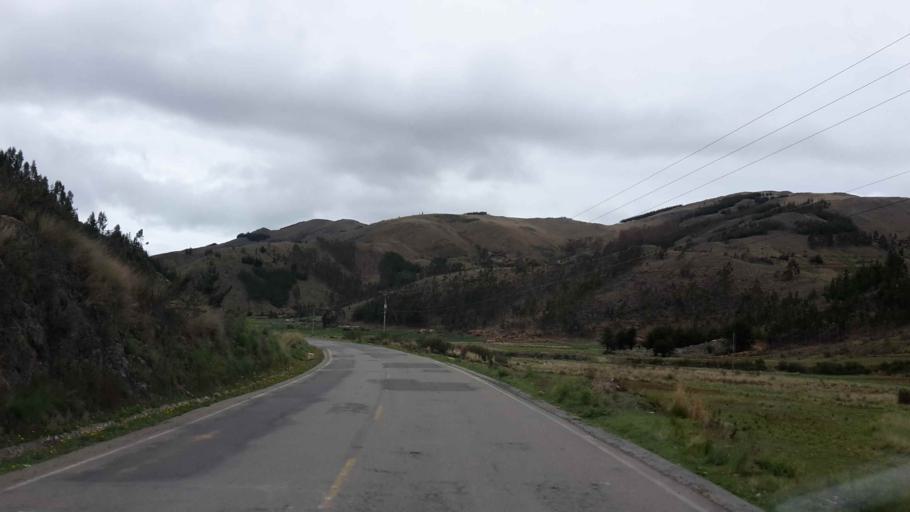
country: BO
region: Cochabamba
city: Arani
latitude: -17.4849
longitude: -65.5557
